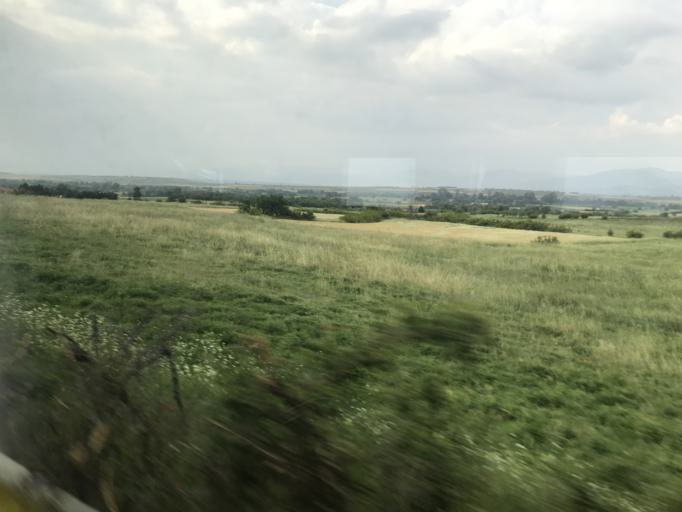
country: GR
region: East Macedonia and Thrace
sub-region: Nomos Rodopis
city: Sapes
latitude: 41.0305
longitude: 25.6823
